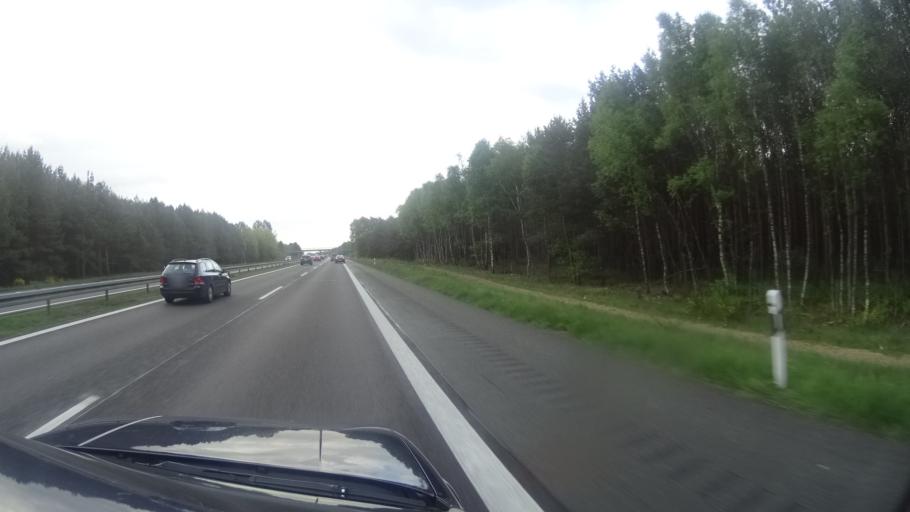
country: DE
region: Brandenburg
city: Walsleben
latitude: 53.0171
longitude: 12.5800
